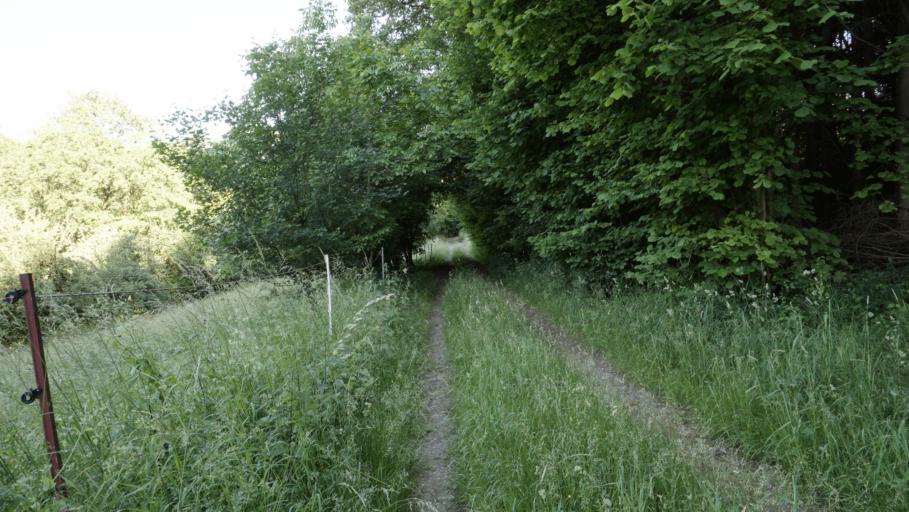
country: DE
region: Baden-Wuerttemberg
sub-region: Karlsruhe Region
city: Billigheim
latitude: 49.3802
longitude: 9.2086
